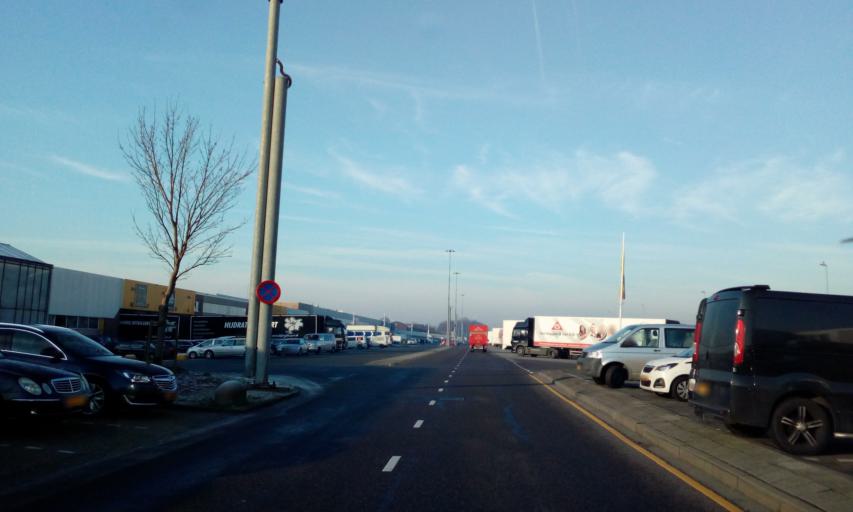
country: NL
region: South Holland
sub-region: Gemeente Lansingerland
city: Bleiswijk
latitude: 52.0299
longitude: 4.5510
